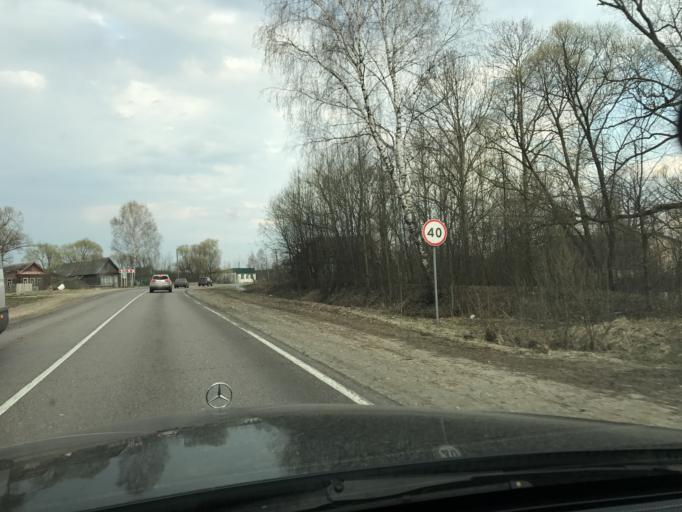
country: RU
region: Vladimir
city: Imeni Vorovskogo
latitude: 55.7790
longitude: 41.2828
